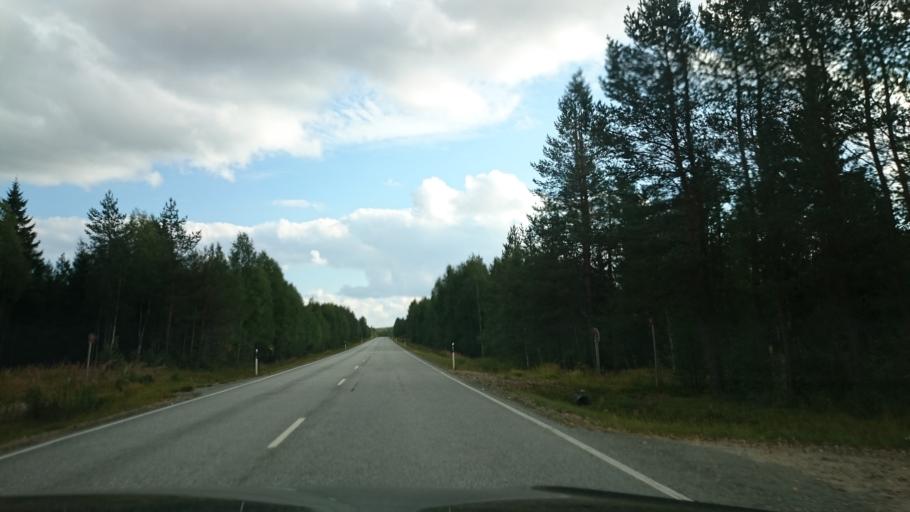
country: FI
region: Kainuu
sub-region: Kehys-Kainuu
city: Kuhmo
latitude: 64.5271
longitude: 29.9452
